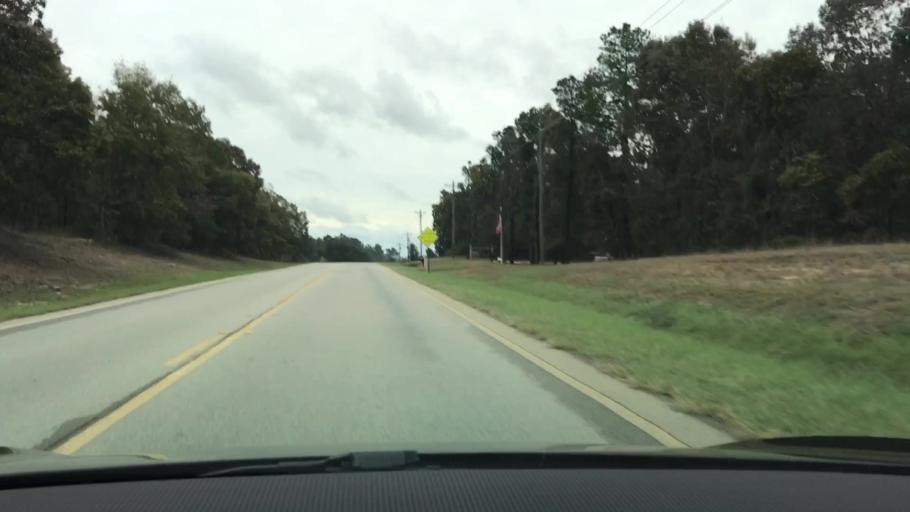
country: US
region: Georgia
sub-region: Jefferson County
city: Wrens
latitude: 33.1915
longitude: -82.4585
